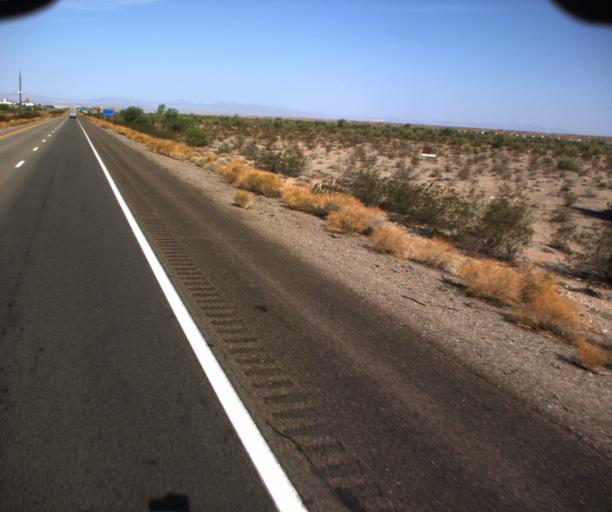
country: US
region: Arizona
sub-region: Mohave County
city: Desert Hills
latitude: 34.7303
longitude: -114.2966
